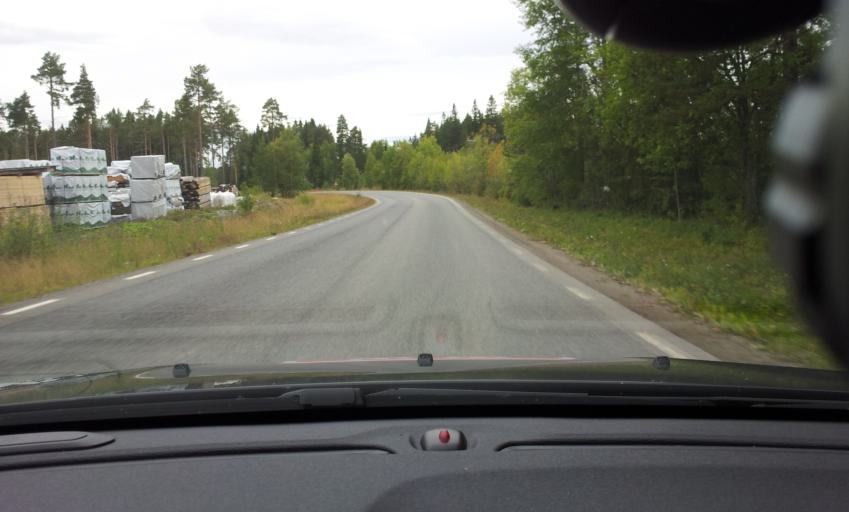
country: SE
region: Jaemtland
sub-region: OEstersunds Kommun
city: Brunflo
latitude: 63.0457
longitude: 14.8655
